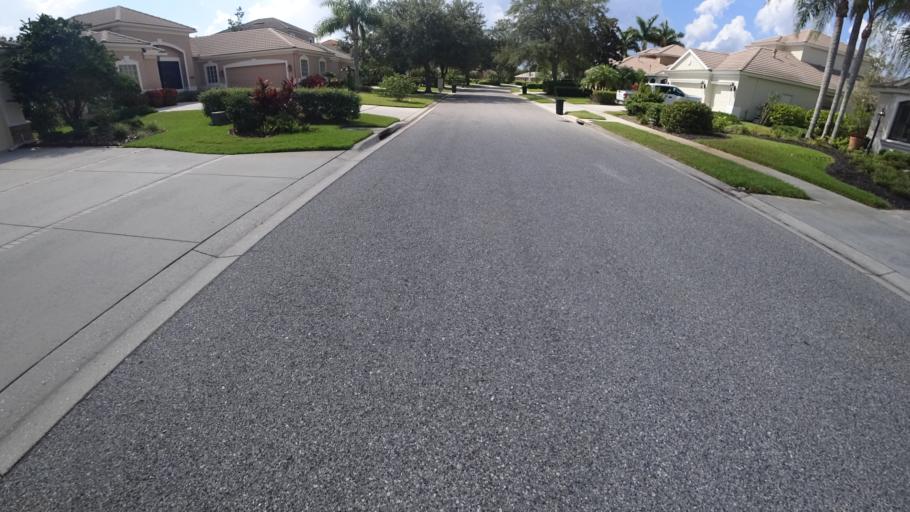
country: US
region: Florida
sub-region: Sarasota County
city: The Meadows
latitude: 27.4182
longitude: -82.4208
